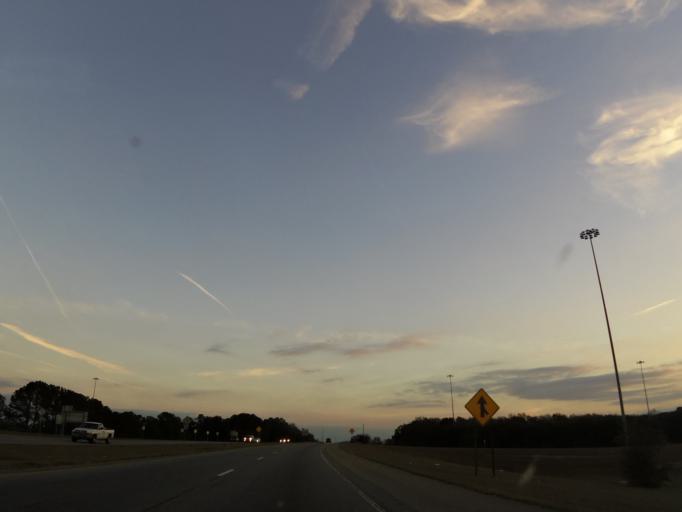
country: US
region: Georgia
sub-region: Dougherty County
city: Albany
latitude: 31.5828
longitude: -84.1123
